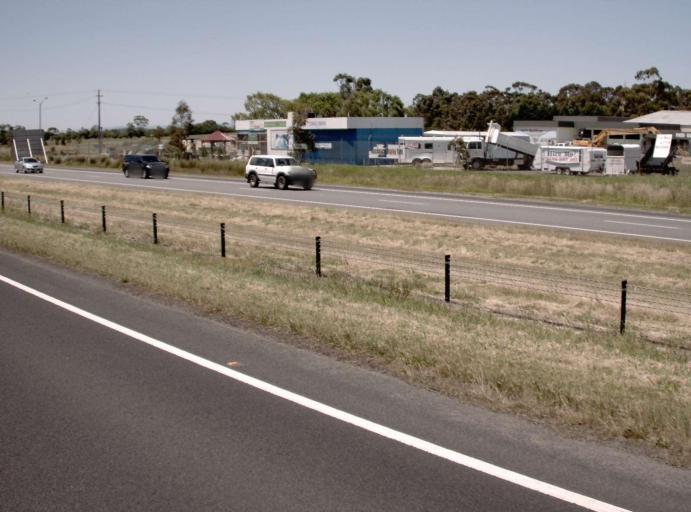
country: AU
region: Victoria
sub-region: Cardinia
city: Pakenham Upper
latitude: -38.0691
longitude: 145.5711
